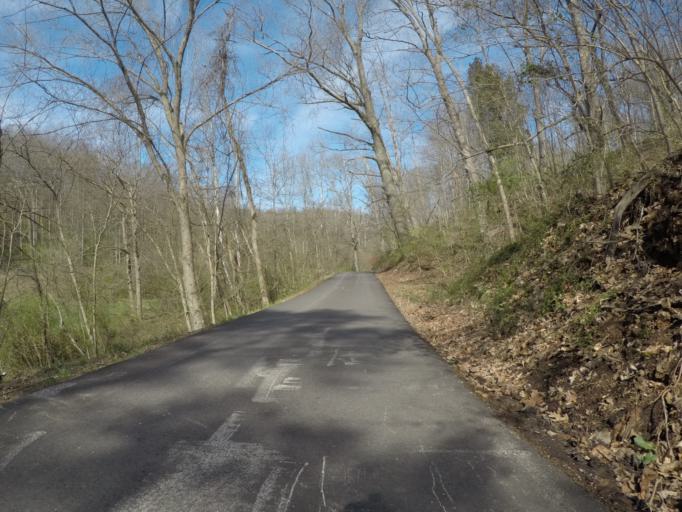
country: US
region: West Virginia
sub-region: Cabell County
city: Pea Ridge
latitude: 38.3933
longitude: -82.3493
